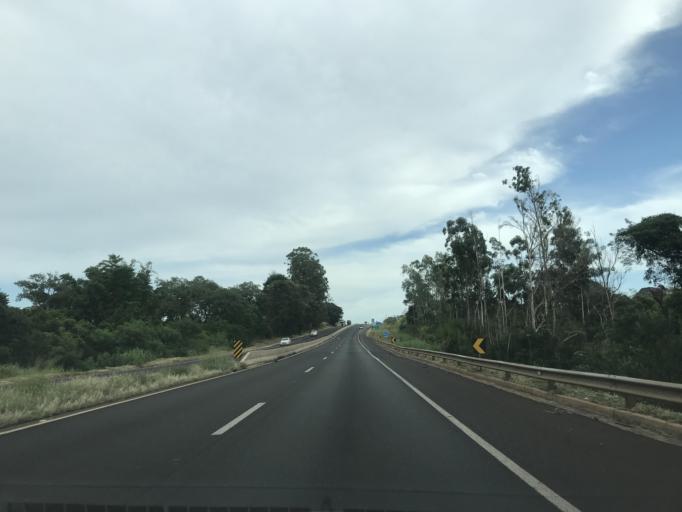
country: BR
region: Parana
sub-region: Alto Parana
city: Alto Parana
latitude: -23.1378
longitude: -52.2899
